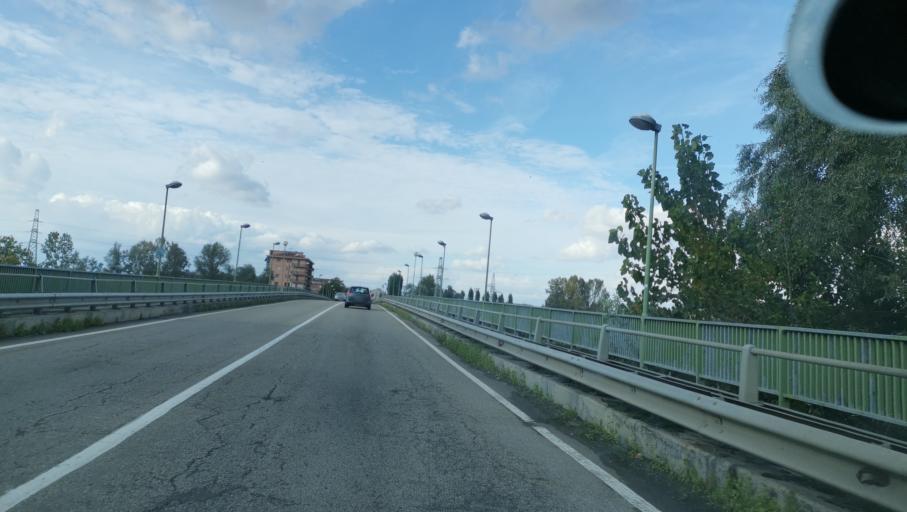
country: IT
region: Piedmont
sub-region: Provincia di Torino
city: Chivasso
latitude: 45.1799
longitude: 7.8905
